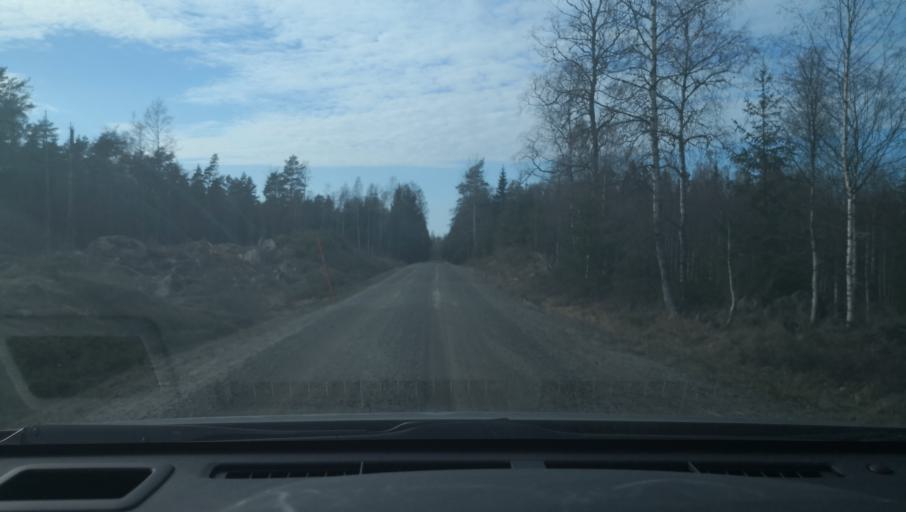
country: SE
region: Uppsala
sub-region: Heby Kommun
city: Heby
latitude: 59.8526
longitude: 16.8729
